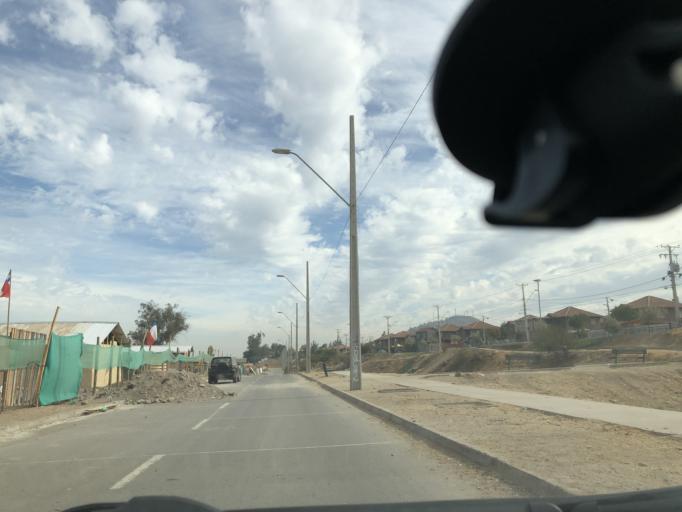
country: CL
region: Santiago Metropolitan
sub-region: Provincia de Cordillera
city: Puente Alto
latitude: -33.6144
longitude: -70.5267
